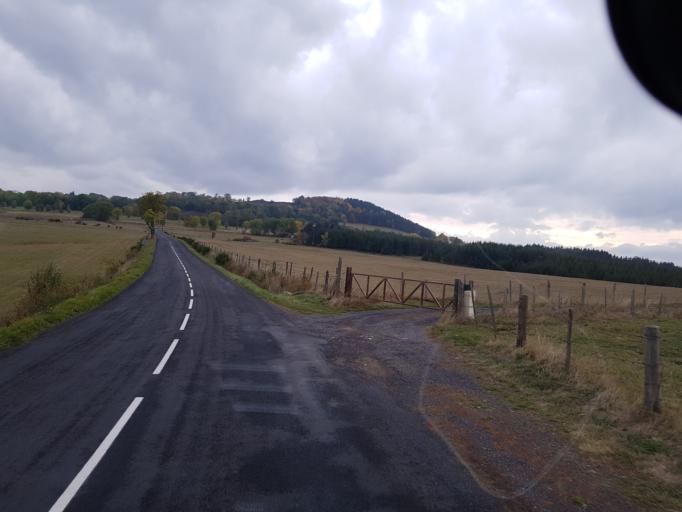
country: FR
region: Languedoc-Roussillon
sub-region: Departement de la Lozere
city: Langogne
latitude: 44.7213
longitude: 3.8320
